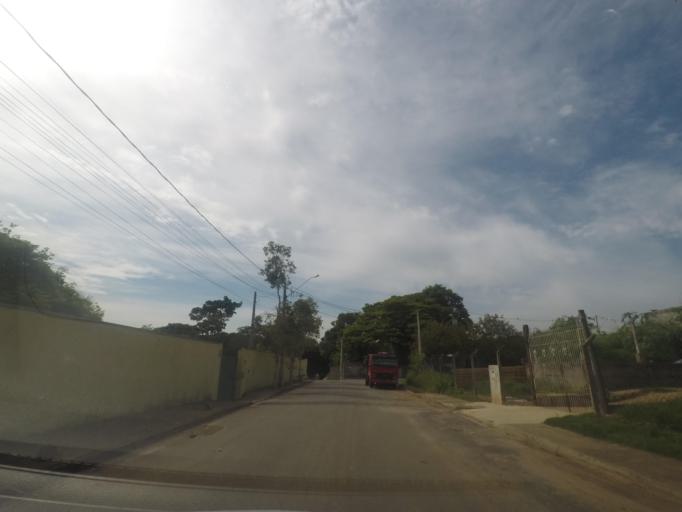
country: BR
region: Sao Paulo
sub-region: Sumare
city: Sumare
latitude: -22.8015
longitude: -47.2445
